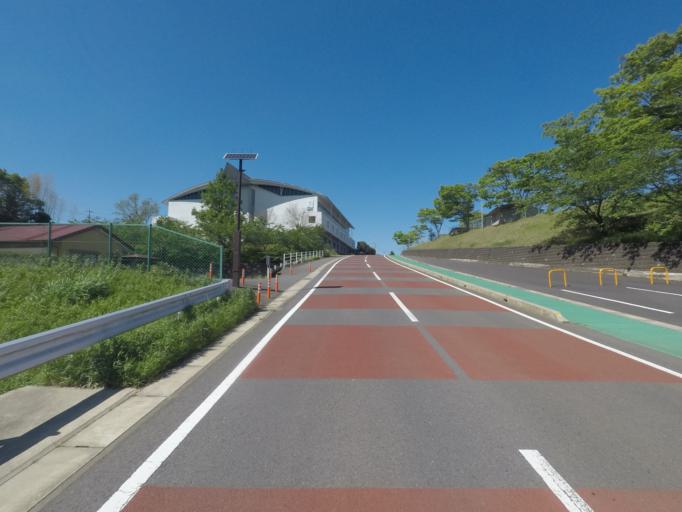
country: JP
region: Ibaraki
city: Itako
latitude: 36.0221
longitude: 140.4750
